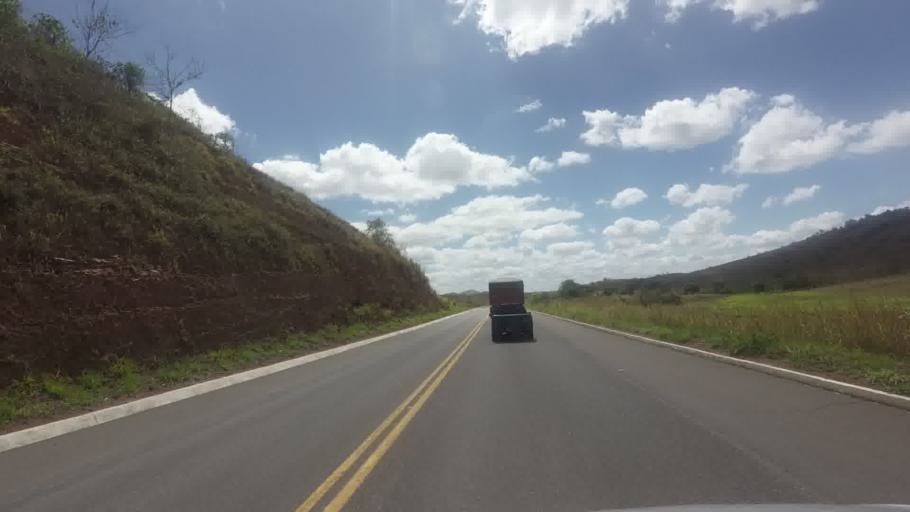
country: BR
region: Minas Gerais
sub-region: Recreio
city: Recreio
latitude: -21.6677
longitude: -42.3876
